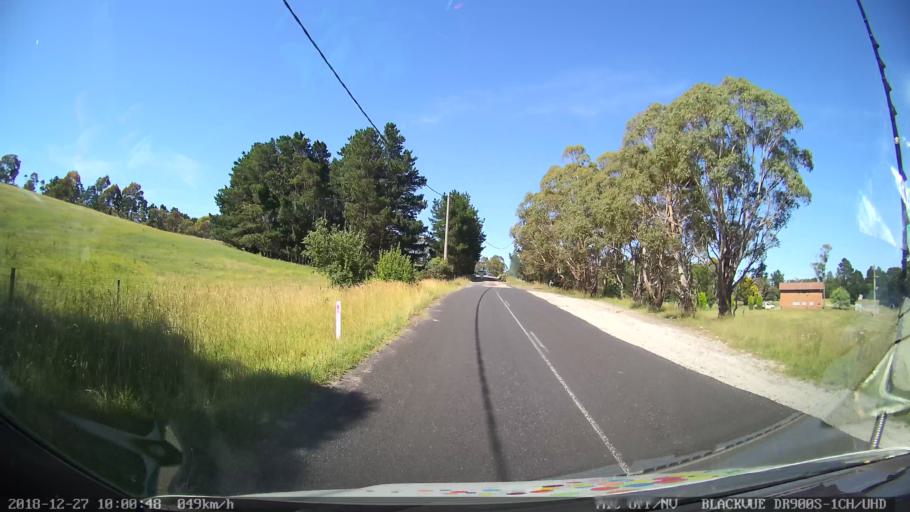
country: AU
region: New South Wales
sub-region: Lithgow
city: Portland
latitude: -33.4391
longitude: 149.9405
